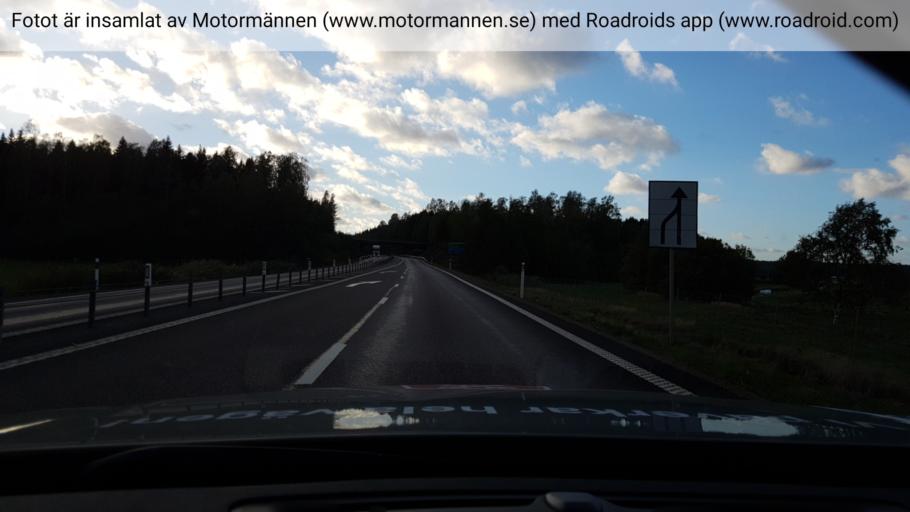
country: SE
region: Vaermland
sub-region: Karlstads Kommun
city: Skattkarr
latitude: 59.4154
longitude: 13.7430
